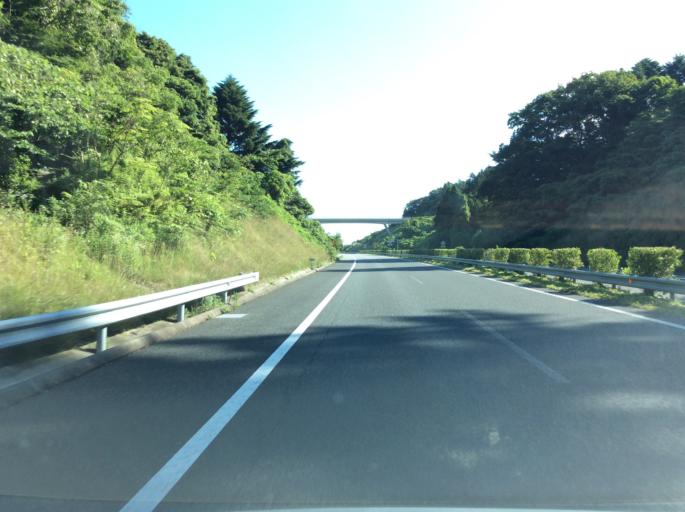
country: JP
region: Fukushima
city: Iwaki
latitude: 37.1870
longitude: 140.9841
